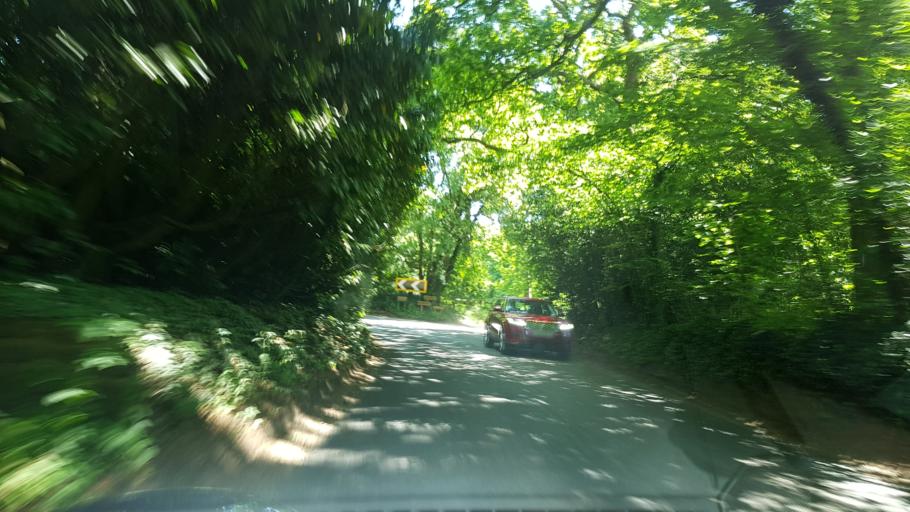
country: GB
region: England
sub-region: Surrey
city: Godalming
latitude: 51.1580
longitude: -0.5834
